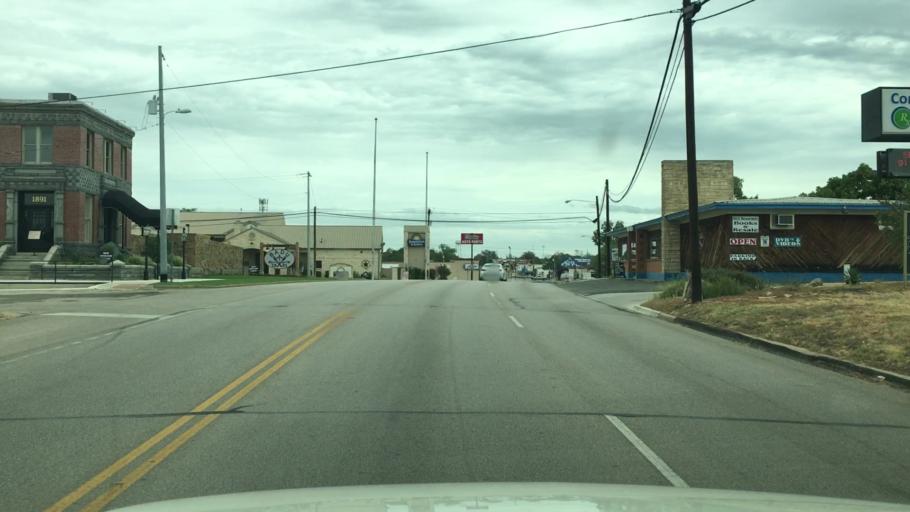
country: US
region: Texas
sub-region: Llano County
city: Llano
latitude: 30.7561
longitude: -98.6757
